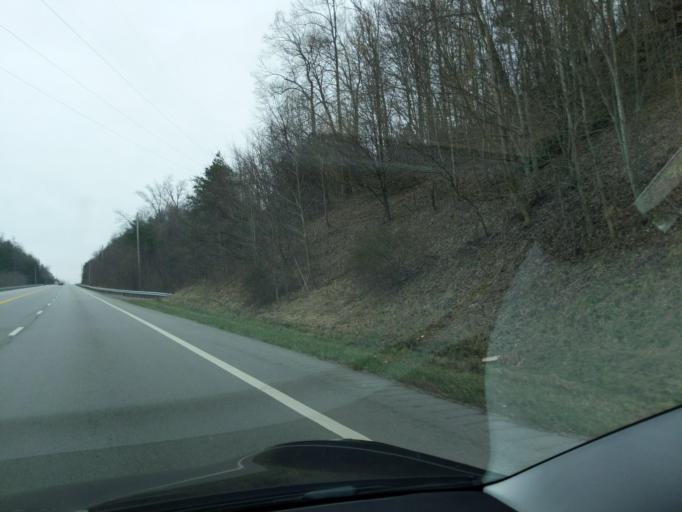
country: US
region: Kentucky
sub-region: Whitley County
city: Corbin
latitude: 36.9188
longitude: -84.1122
